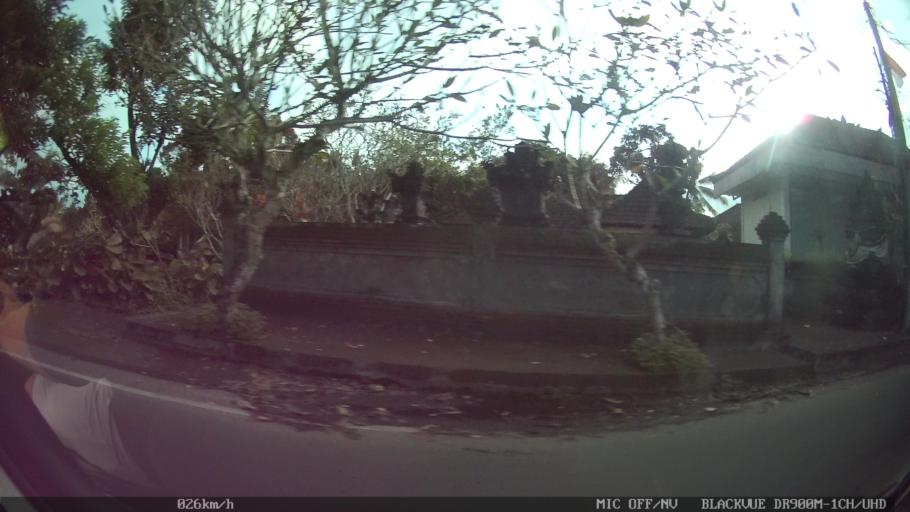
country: ID
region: Bali
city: Banjar Pande
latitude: -8.5129
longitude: 115.2498
